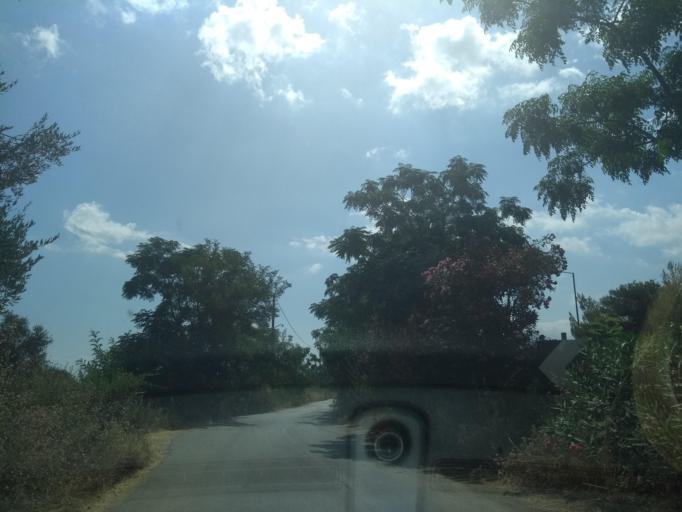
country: GR
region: Crete
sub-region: Nomos Chanias
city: Georgioupolis
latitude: 35.3574
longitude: 24.2663
